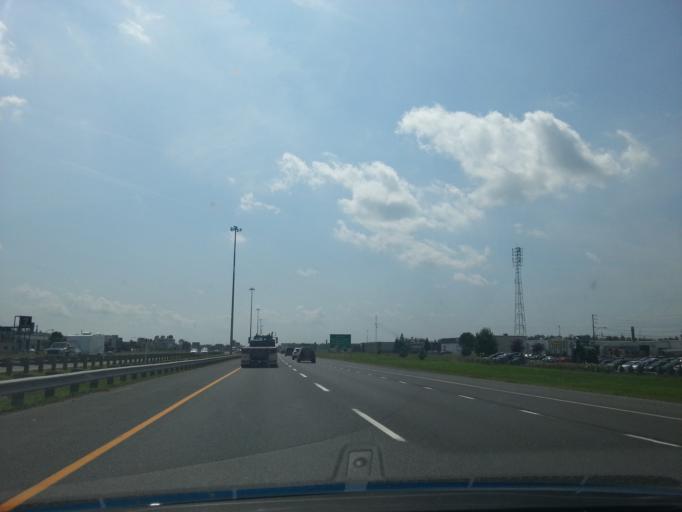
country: CA
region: Quebec
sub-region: Centre-du-Quebec
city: Drummondville
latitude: 45.8979
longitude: -72.5300
